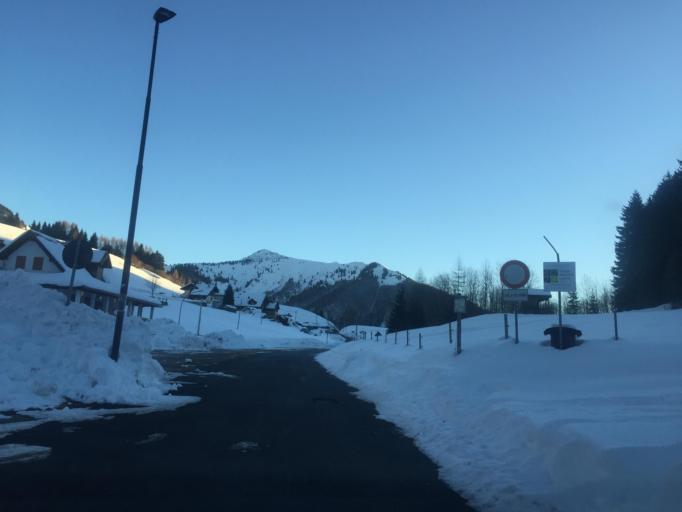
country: IT
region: Friuli Venezia Giulia
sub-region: Provincia di Udine
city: Lauco
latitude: 46.4611
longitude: 12.9318
